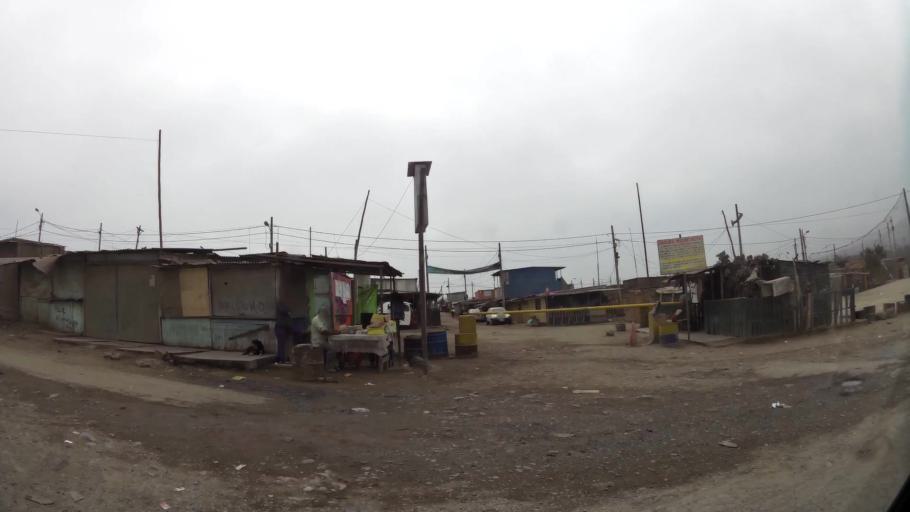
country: PE
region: Lima
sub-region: Lima
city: Surco
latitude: -12.2392
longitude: -76.9283
